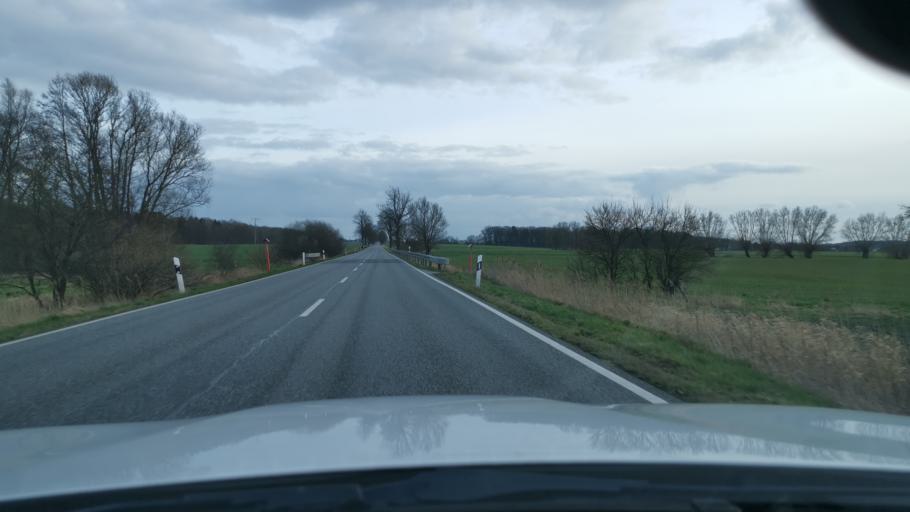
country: DE
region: Mecklenburg-Vorpommern
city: Dummerstorf
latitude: 53.9940
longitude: 12.2669
